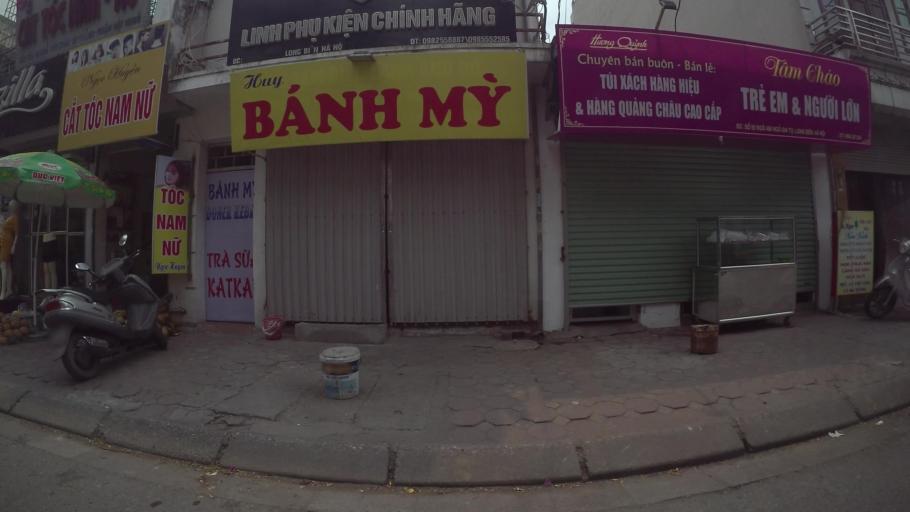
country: VN
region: Ha Noi
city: Trau Quy
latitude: 21.0691
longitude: 105.9072
